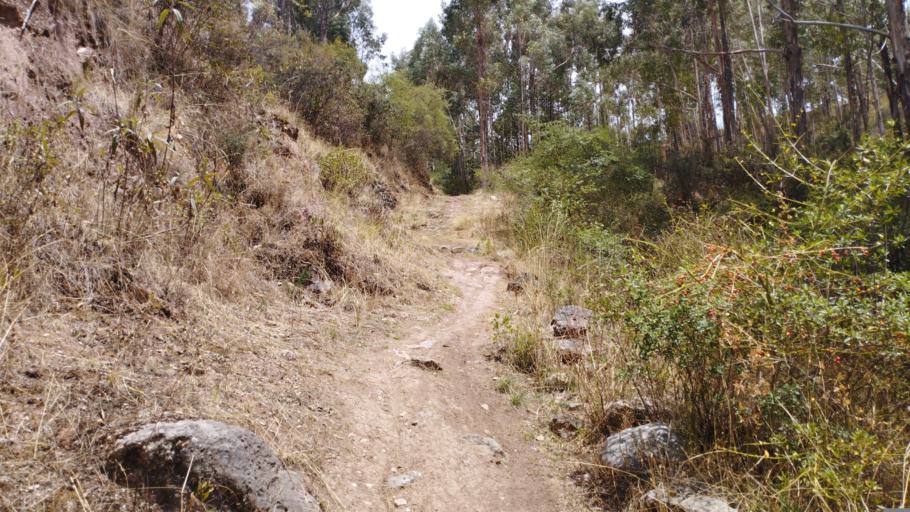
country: PE
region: Cusco
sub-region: Provincia de Cusco
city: Cusco
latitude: -13.5185
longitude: -71.9438
